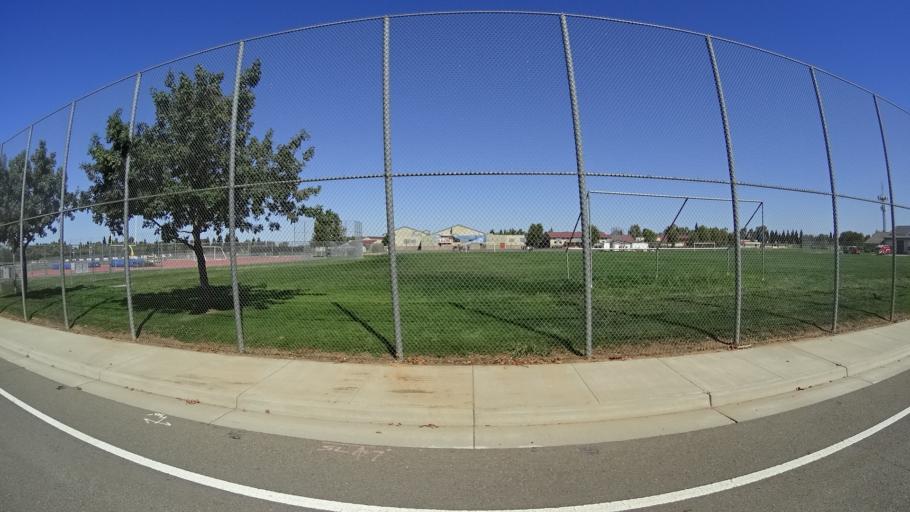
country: US
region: California
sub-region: Sacramento County
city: Elk Grove
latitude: 38.4237
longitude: -121.3405
